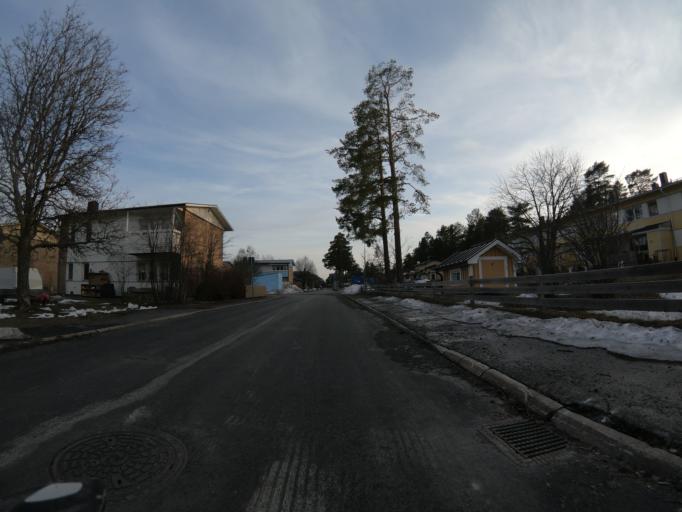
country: SE
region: Vaesterbotten
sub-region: Umea Kommun
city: Umea
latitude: 63.8433
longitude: 20.2830
